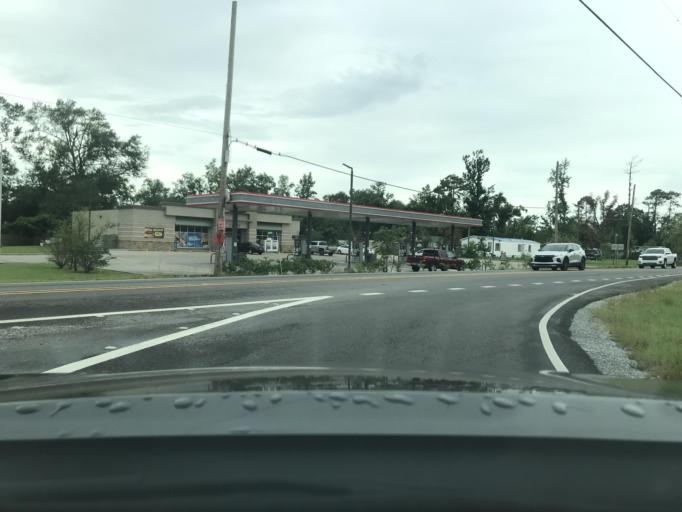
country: US
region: Louisiana
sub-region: Calcasieu Parish
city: Westlake
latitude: 30.2851
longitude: -93.2499
